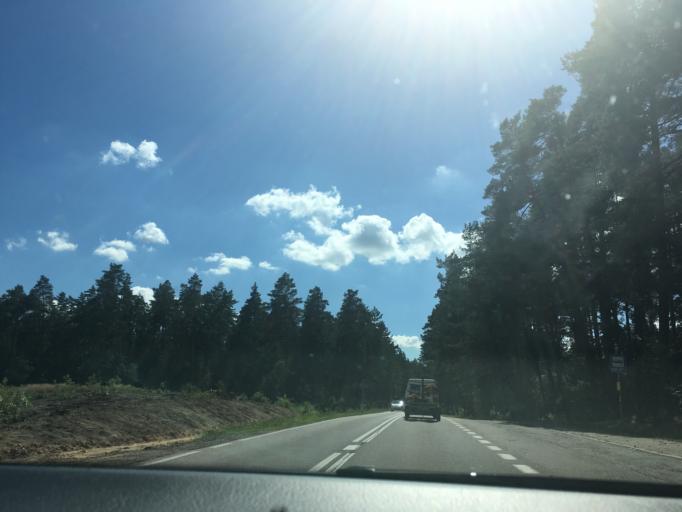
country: PL
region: Podlasie
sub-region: Powiat augustowski
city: Augustow
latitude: 53.8492
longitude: 23.0471
